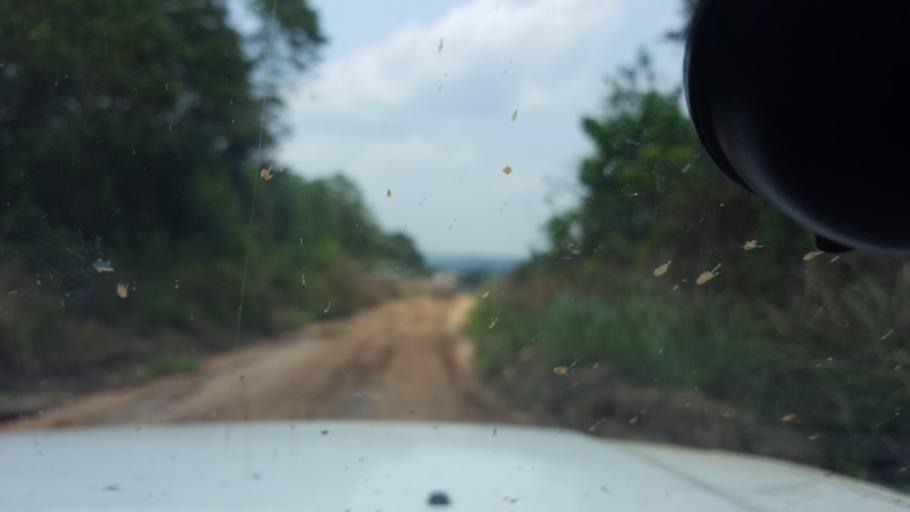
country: CD
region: Bandundu
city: Mushie
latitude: -3.7514
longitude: 16.6389
